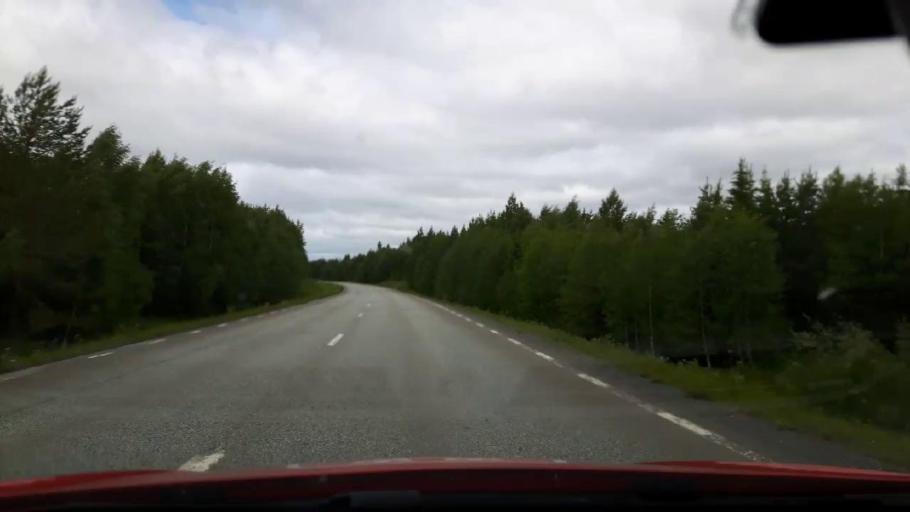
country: SE
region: Jaemtland
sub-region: Krokoms Kommun
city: Krokom
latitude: 63.3851
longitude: 14.5075
